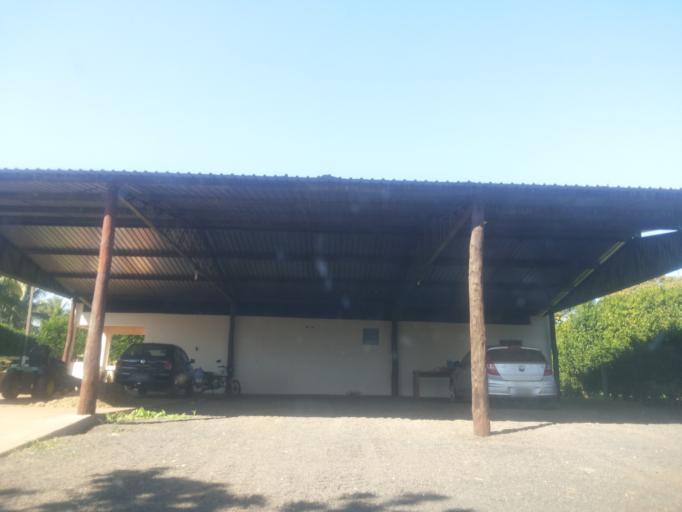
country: BR
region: Minas Gerais
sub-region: Santa Vitoria
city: Santa Vitoria
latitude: -19.0030
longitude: -50.4328
